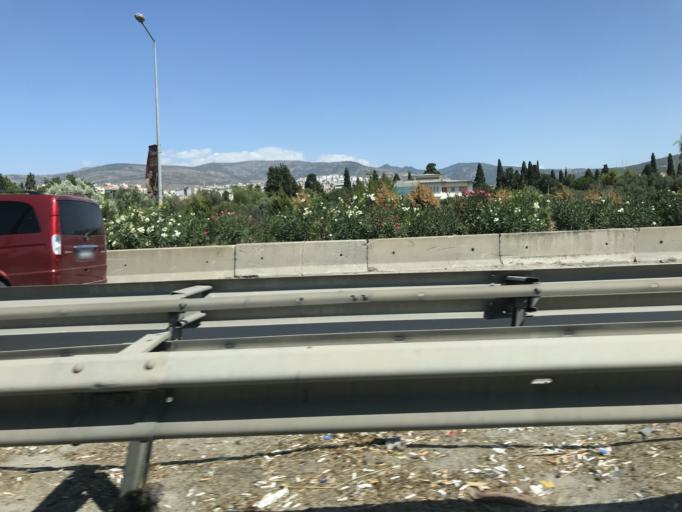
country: TR
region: Izmir
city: Bornova
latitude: 38.4595
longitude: 27.2210
